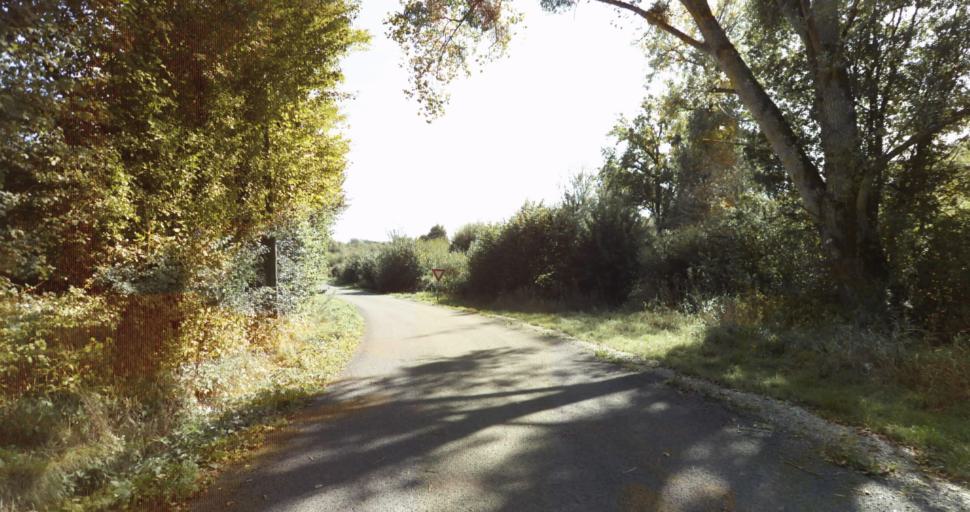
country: FR
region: Lower Normandy
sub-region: Departement de l'Orne
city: Gace
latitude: 48.7322
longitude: 0.2366
